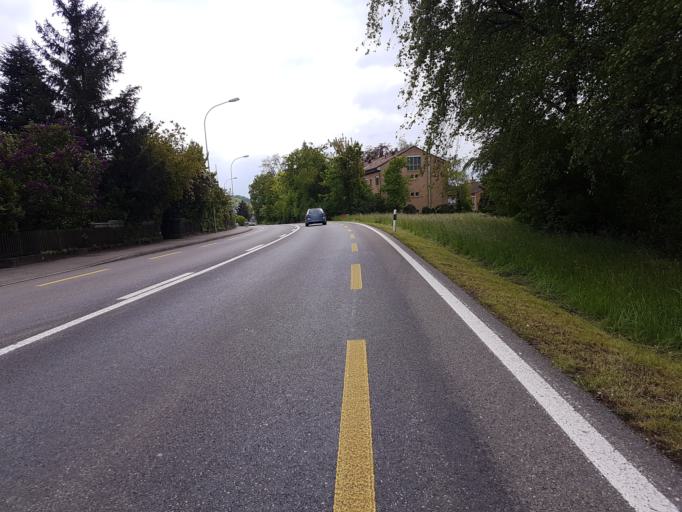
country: CH
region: Aargau
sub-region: Bezirk Brugg
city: Schinznach Bad
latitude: 47.4545
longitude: 8.1681
